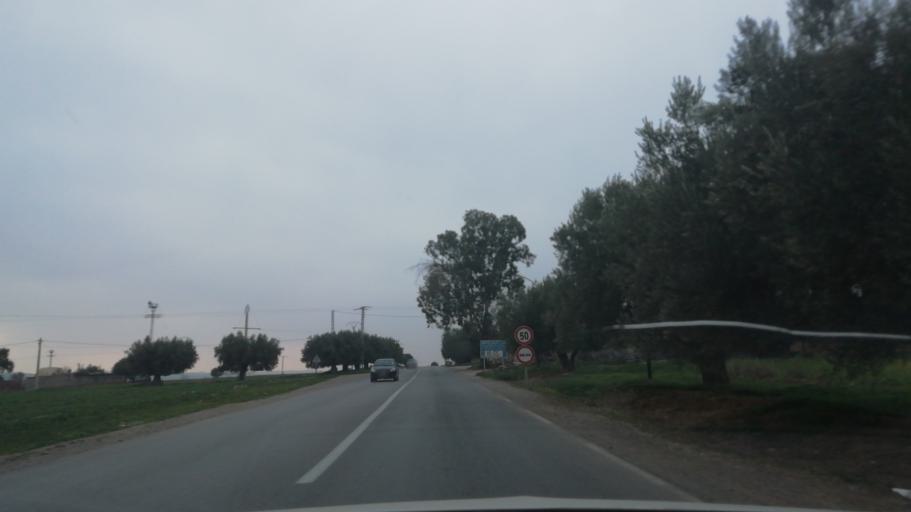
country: DZ
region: Sidi Bel Abbes
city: Sfizef
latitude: 35.2542
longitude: -0.1901
